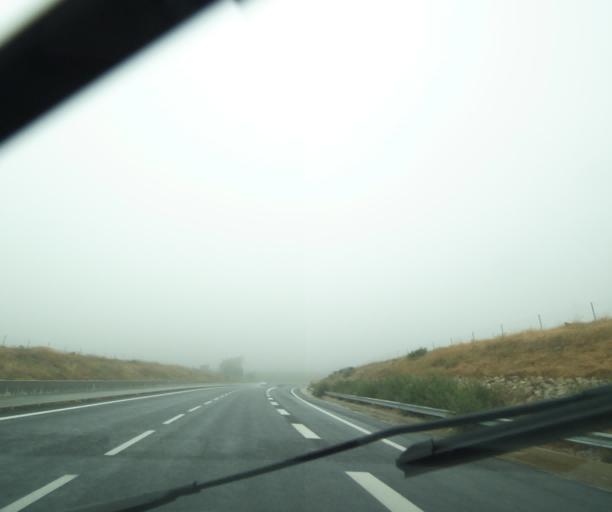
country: FR
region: Midi-Pyrenees
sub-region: Departement de l'Aveyron
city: Naucelle
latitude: 44.1853
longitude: 2.3566
